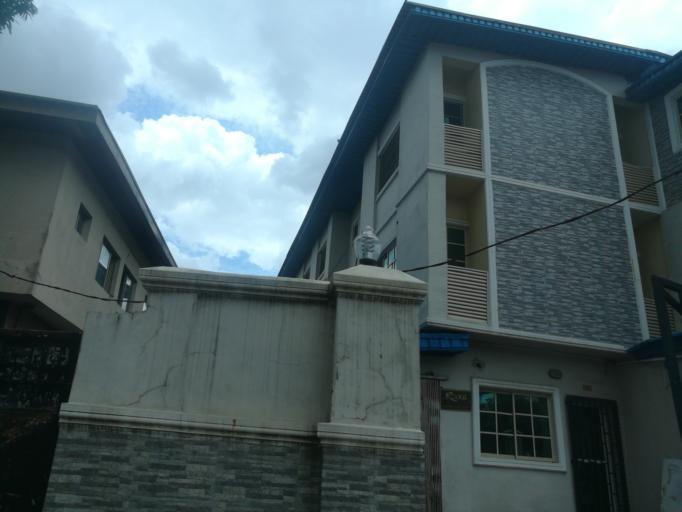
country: NG
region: Lagos
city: Ikeja
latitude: 6.5992
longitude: 3.3497
